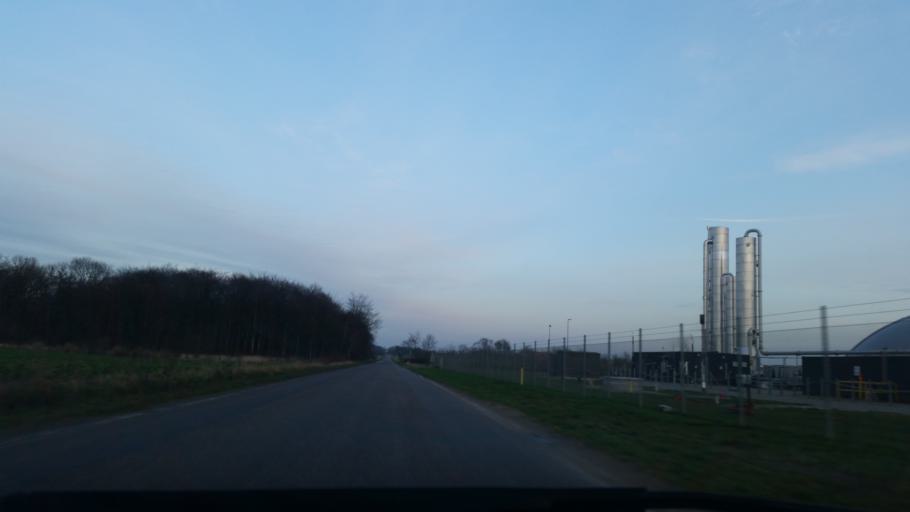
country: DK
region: South Denmark
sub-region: Vejen Kommune
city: Rodding
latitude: 55.3834
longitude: 8.9581
